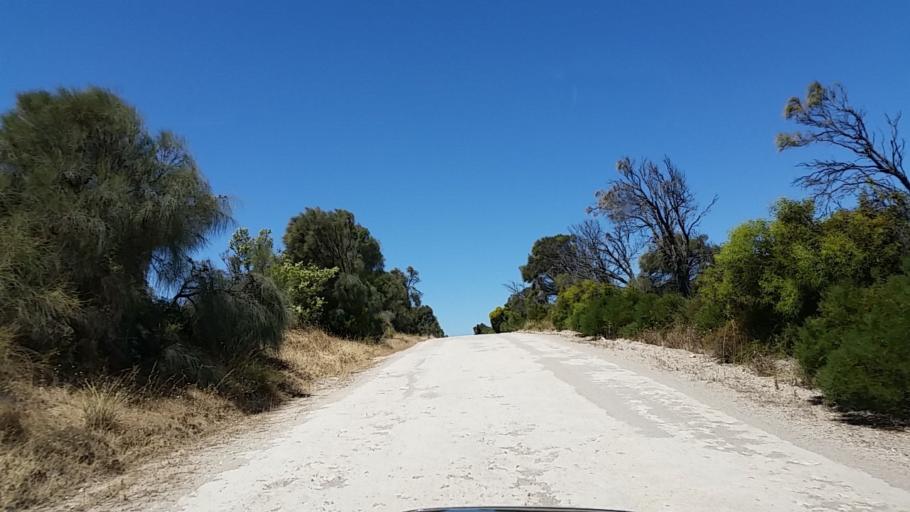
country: AU
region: South Australia
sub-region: Yorke Peninsula
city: Honiton
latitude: -35.0934
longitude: 137.4340
